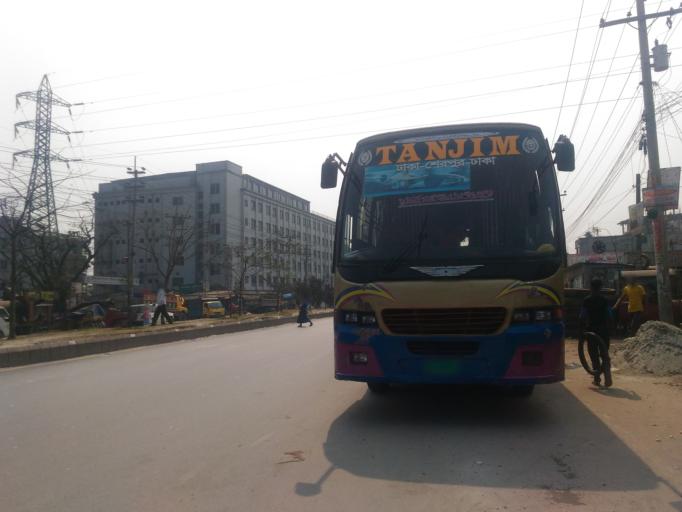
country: BD
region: Dhaka
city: Tungi
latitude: 23.9985
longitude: 90.3826
